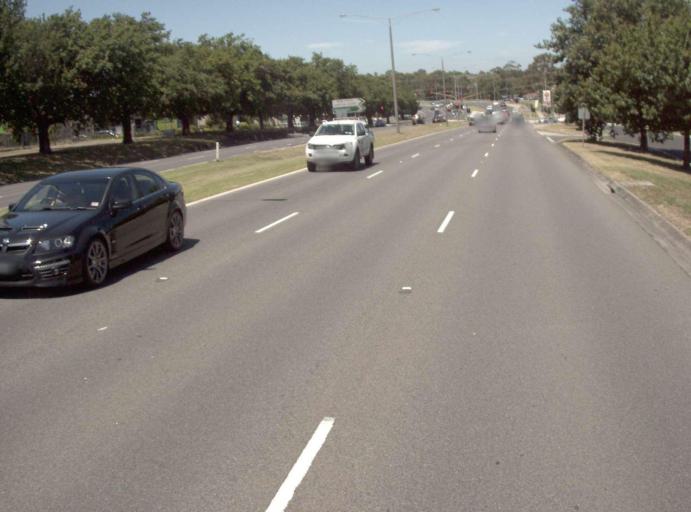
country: AU
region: Victoria
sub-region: Casey
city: Narre Warren
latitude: -38.0240
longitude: 145.3033
